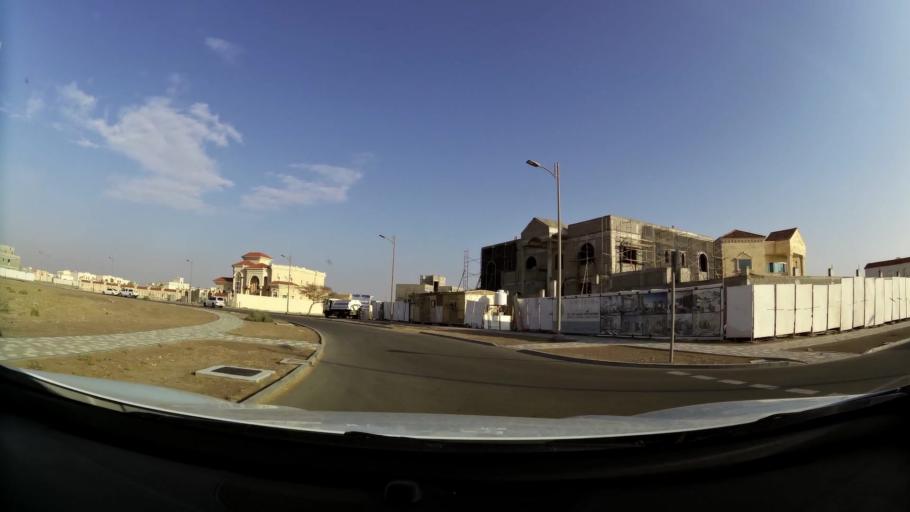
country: AE
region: Abu Dhabi
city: Al Ain
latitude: 24.1045
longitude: 55.8499
